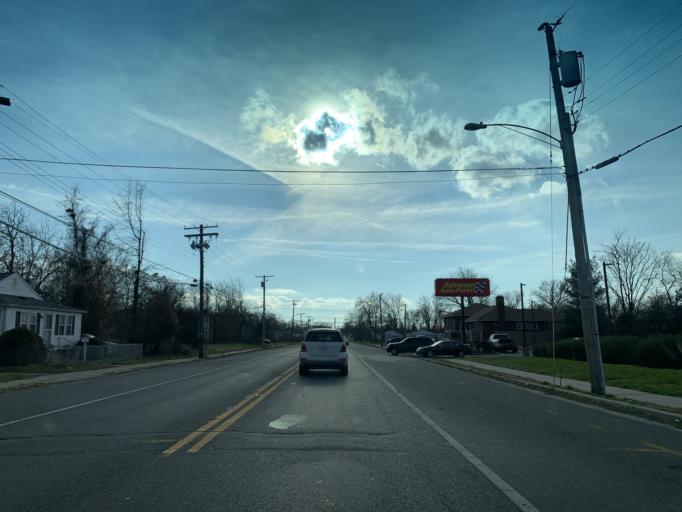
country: US
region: New Jersey
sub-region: Salem County
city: Penns Grove
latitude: 39.7247
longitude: -75.4651
